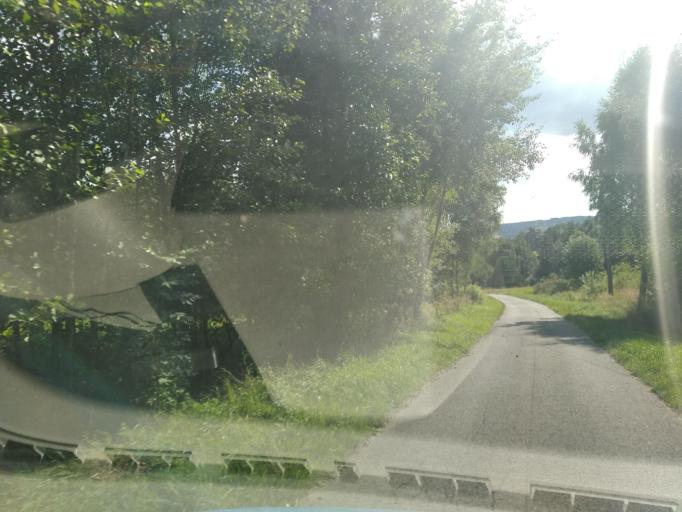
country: PL
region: Subcarpathian Voivodeship
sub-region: Powiat strzyzowski
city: Polomia
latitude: 49.9018
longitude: 21.9205
